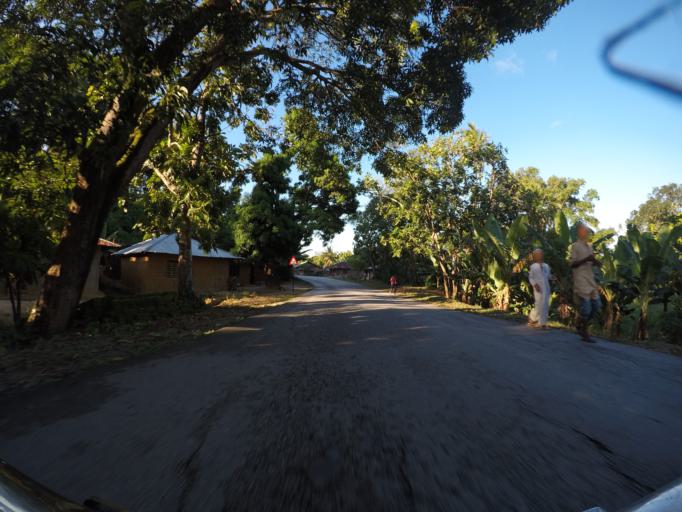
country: TZ
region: Pemba South
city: Mtambile
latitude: -5.3754
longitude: 39.6946
